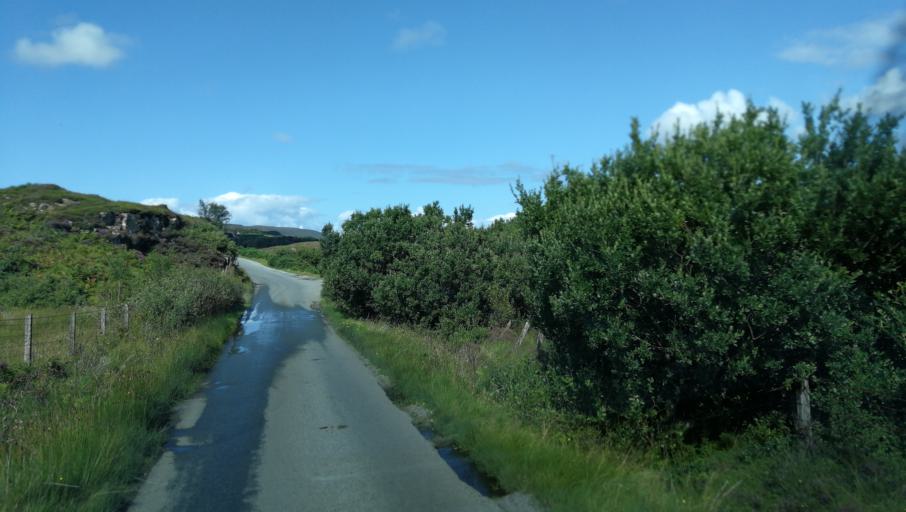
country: GB
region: Scotland
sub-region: Highland
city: Isle of Skye
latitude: 57.4372
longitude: -6.6287
